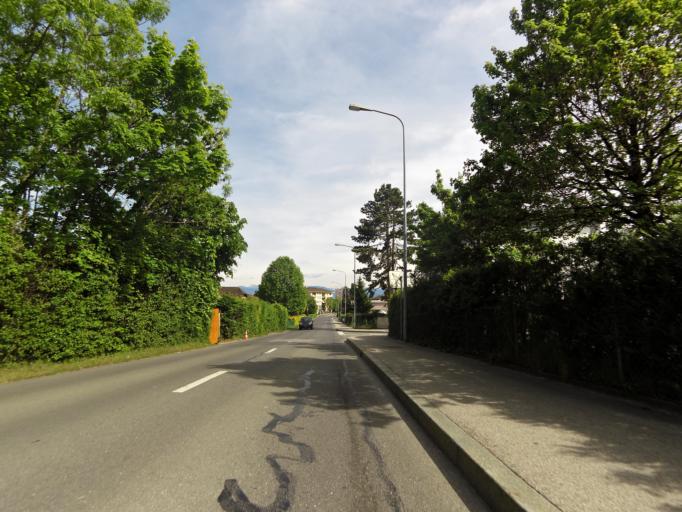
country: CH
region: Vaud
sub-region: Nyon District
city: Nyon
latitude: 46.3946
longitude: 6.2286
